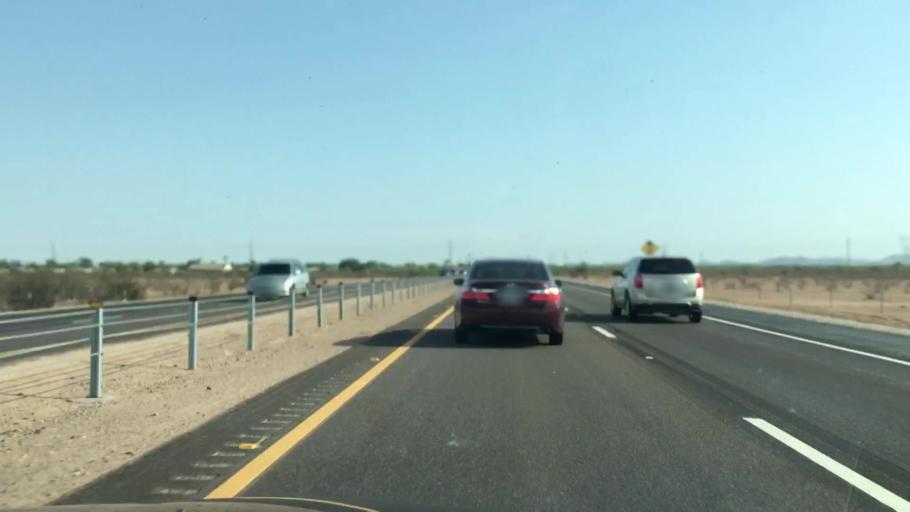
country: US
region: Arizona
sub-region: Maricopa County
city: Queen Creek
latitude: 33.2829
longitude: -111.5634
